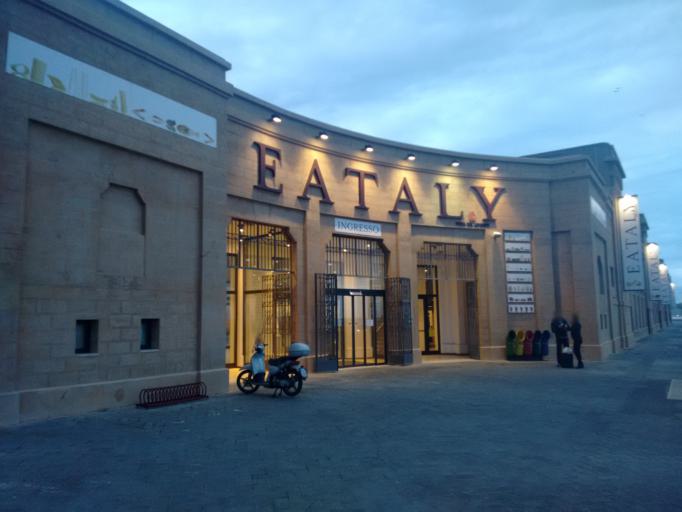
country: IT
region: Apulia
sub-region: Provincia di Bari
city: Bari
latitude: 41.1375
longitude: 16.8381
